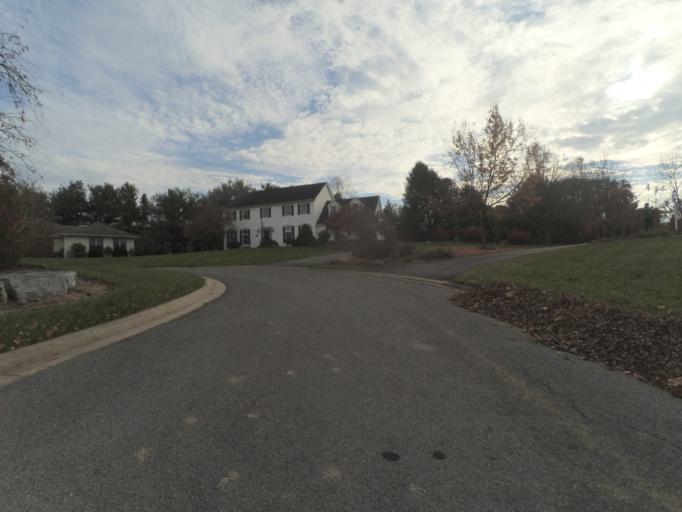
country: US
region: Pennsylvania
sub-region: Centre County
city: Boalsburg
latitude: 40.7749
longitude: -77.8120
